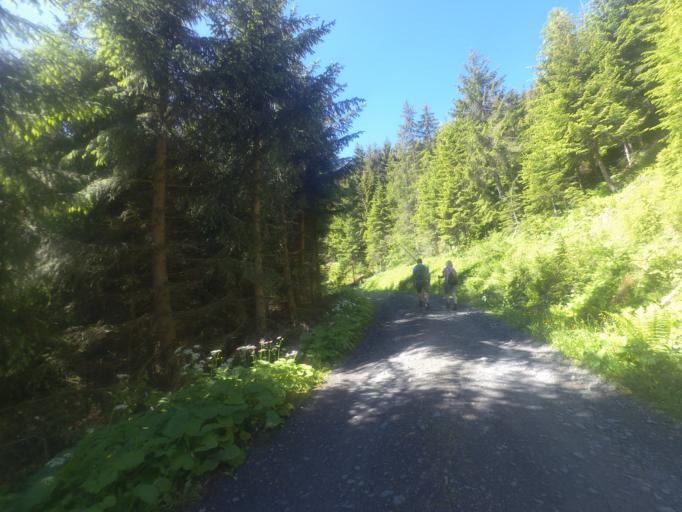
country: AT
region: Salzburg
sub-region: Politischer Bezirk Zell am See
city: Lend
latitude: 47.3258
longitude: 13.0520
